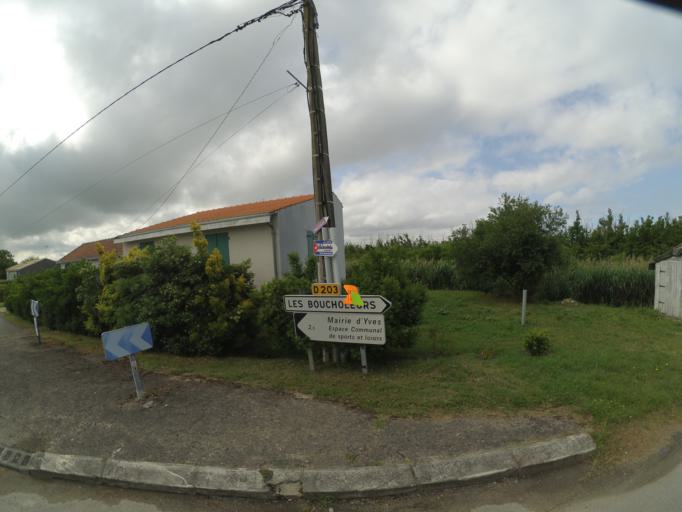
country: FR
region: Poitou-Charentes
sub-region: Departement de la Charente-Maritime
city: Chatelaillon-Plage
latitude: 46.0574
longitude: -1.0615
